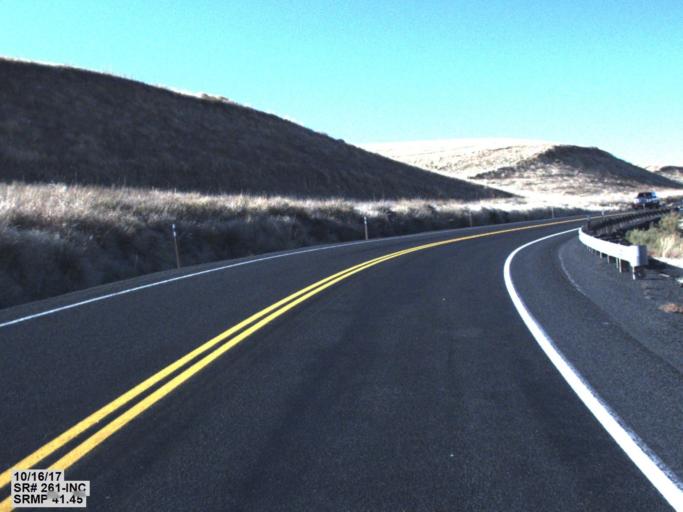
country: US
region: Washington
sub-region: Adams County
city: Ritzville
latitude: 46.8218
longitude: -118.3208
